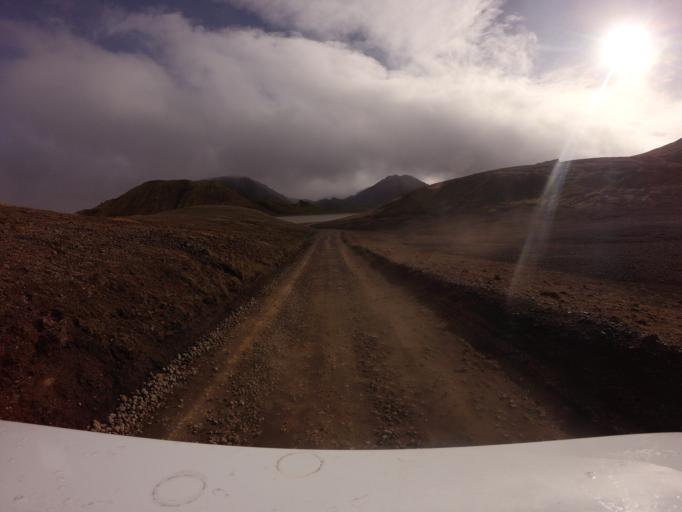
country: IS
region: South
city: Vestmannaeyjar
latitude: 64.0014
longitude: -18.9909
